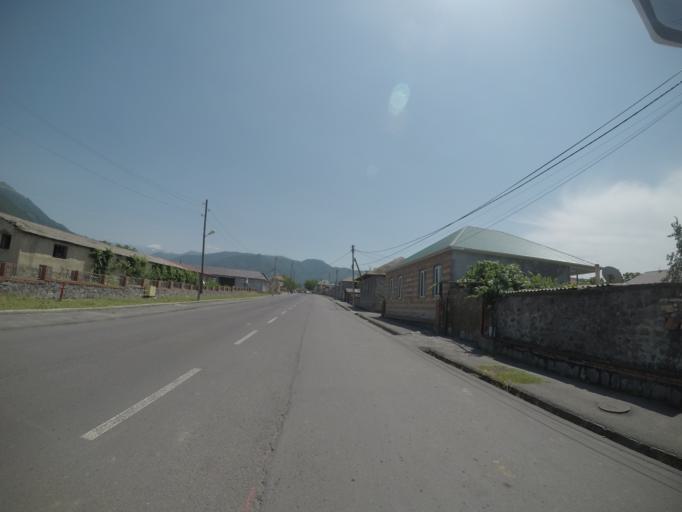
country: AZ
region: Qakh Rayon
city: Qax
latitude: 41.4147
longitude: 46.9094
